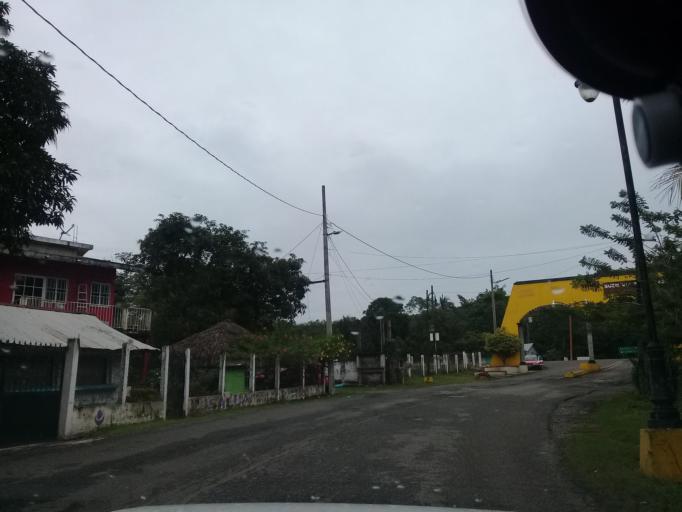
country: MX
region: Veracruz
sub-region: Chalma
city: San Pedro Coyutla
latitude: 21.2096
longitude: -98.3887
